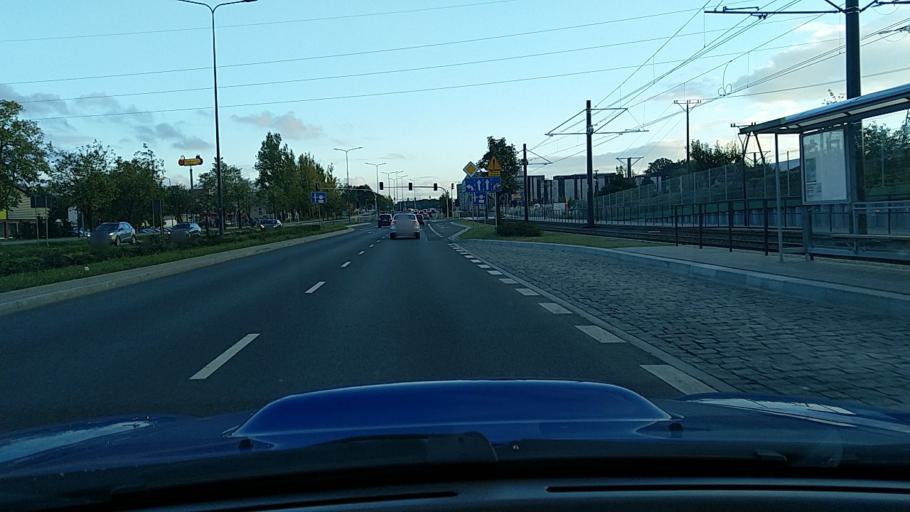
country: PL
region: Warmian-Masurian Voivodeship
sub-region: Powiat olsztynski
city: Olsztyn
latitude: 53.7589
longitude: 20.4866
